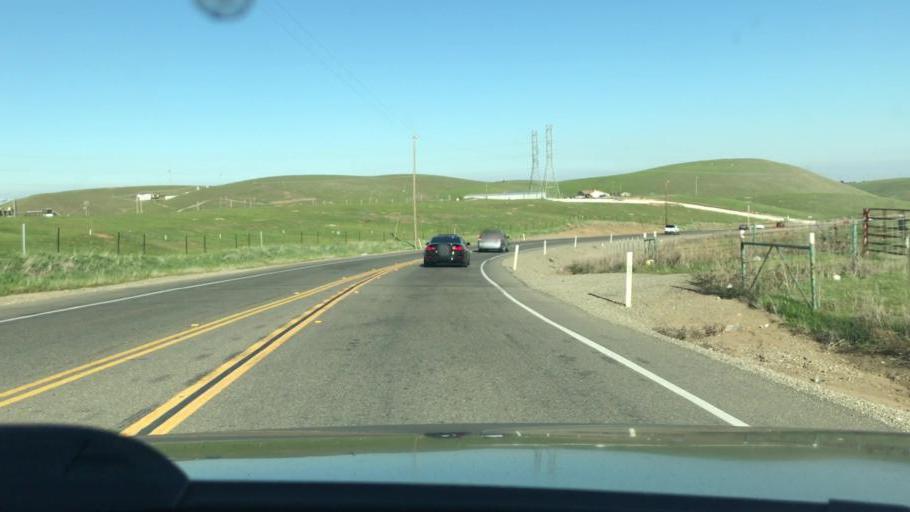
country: US
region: California
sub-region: San Joaquin County
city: Mountain House
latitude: 37.7445
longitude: -121.6010
